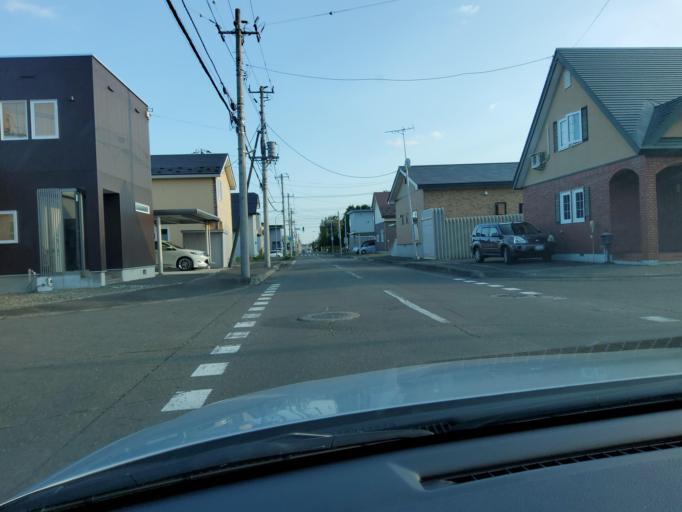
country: JP
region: Hokkaido
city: Obihiro
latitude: 42.9415
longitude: 143.1823
